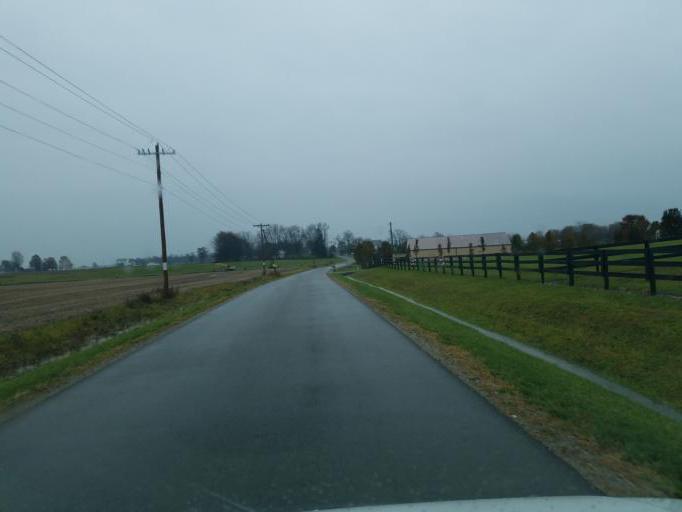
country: US
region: Ohio
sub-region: Knox County
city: Centerburg
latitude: 40.2660
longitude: -82.7354
